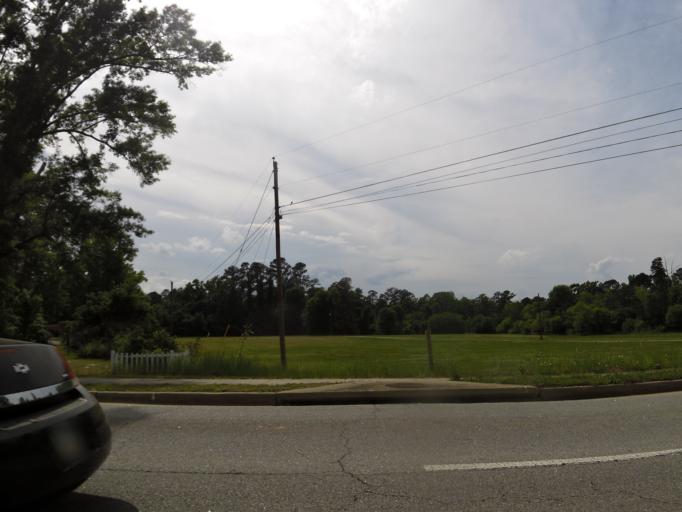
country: US
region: Georgia
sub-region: McDuffie County
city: Thomson
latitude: 33.4763
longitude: -82.5061
